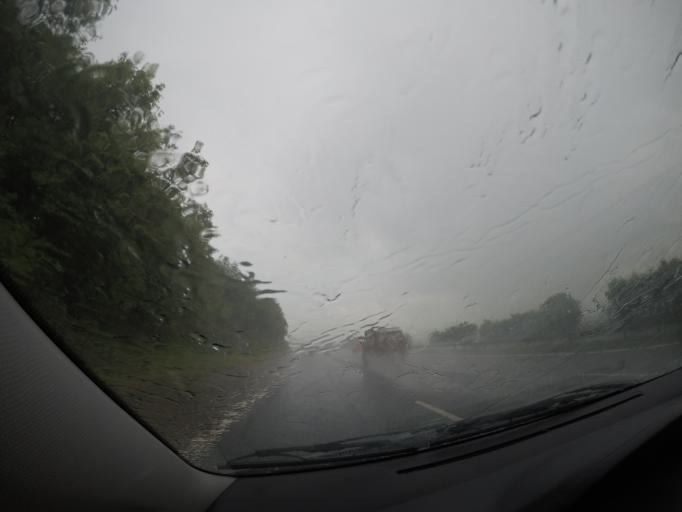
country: GB
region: England
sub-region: Cumbria
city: Penrith
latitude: 54.6996
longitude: -2.7914
